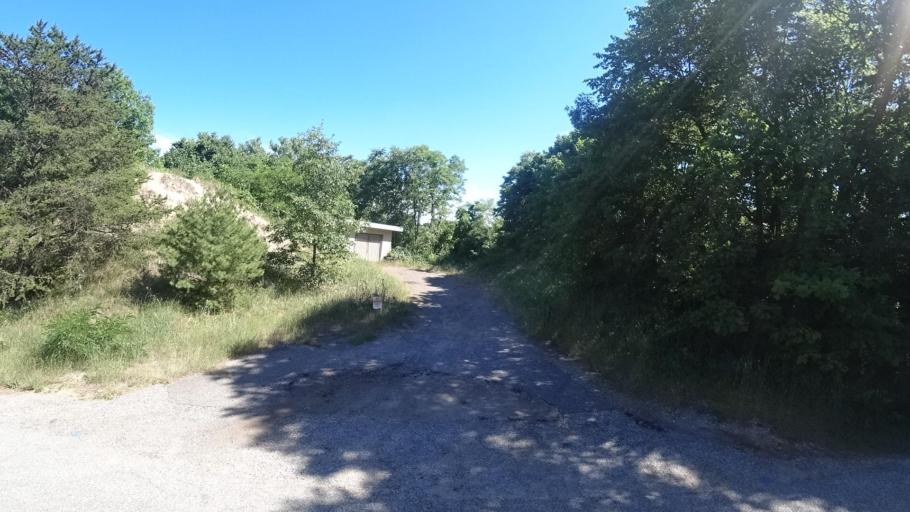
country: US
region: Indiana
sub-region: Porter County
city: Porter
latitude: 41.6588
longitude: -87.0712
